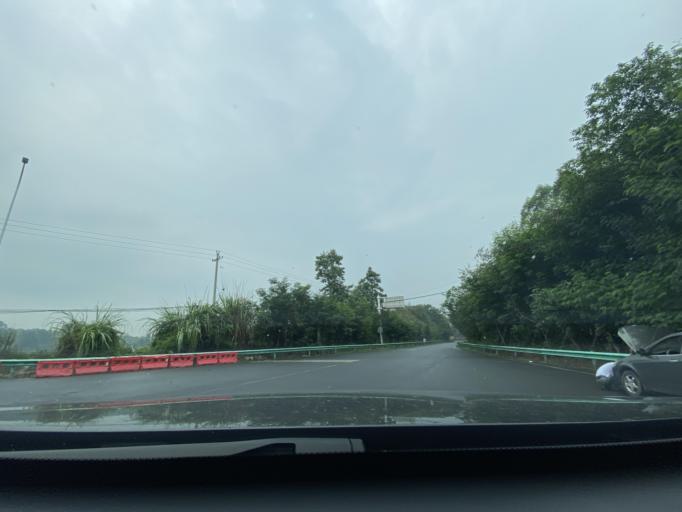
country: CN
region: Sichuan
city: Wenlin
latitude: 30.2949
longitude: 104.1203
